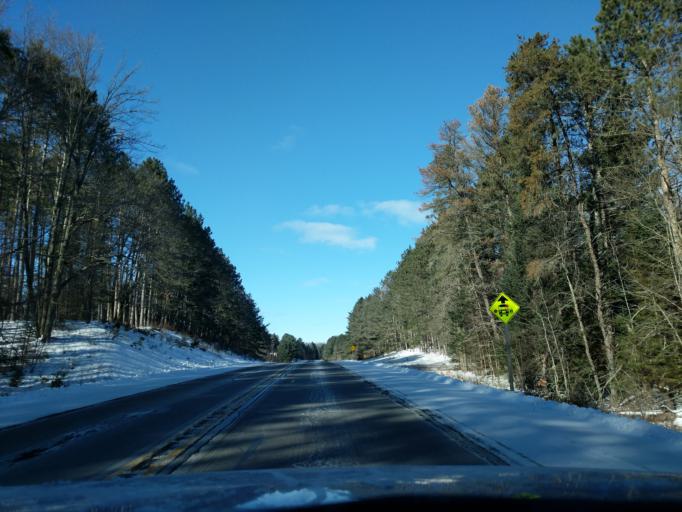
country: US
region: Wisconsin
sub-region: Menominee County
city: Keshena
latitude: 45.1362
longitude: -88.6749
